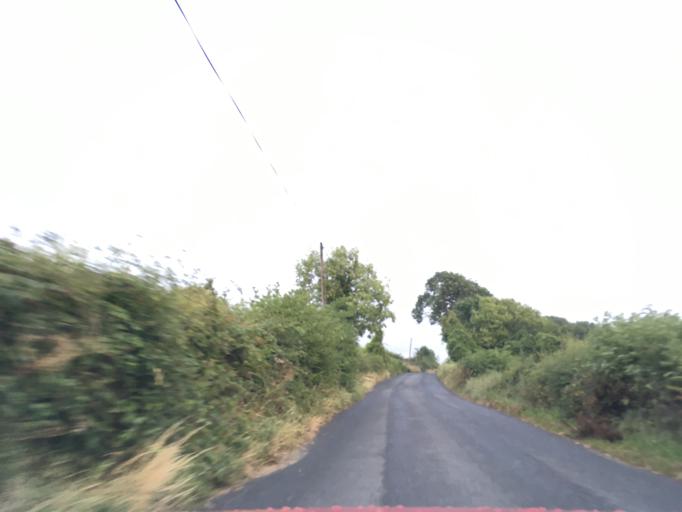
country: IE
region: Munster
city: Cashel
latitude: 52.4695
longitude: -7.9777
